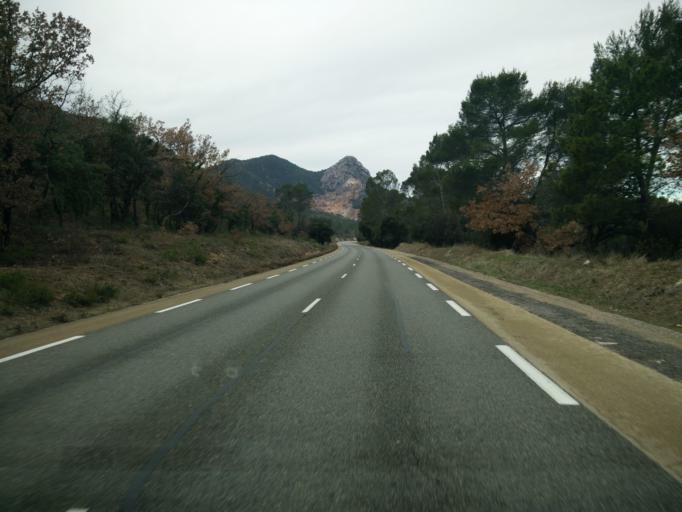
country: FR
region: Provence-Alpes-Cote d'Azur
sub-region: Departement du Var
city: Brignoles
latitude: 43.3801
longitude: 6.0664
